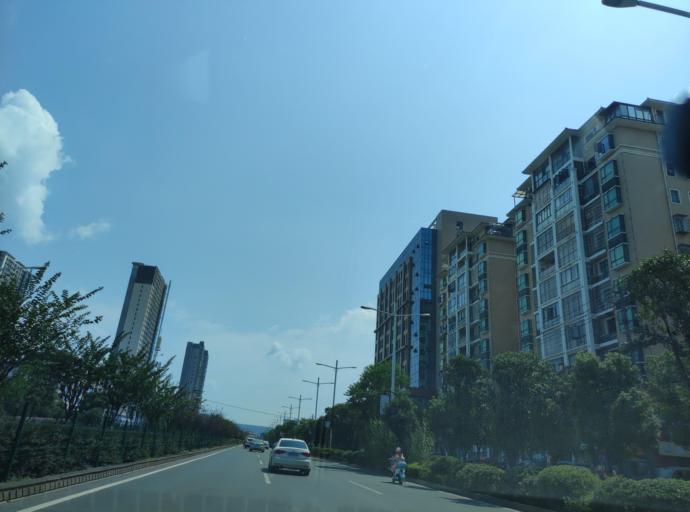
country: CN
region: Jiangxi Sheng
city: Pingxiang
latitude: 27.6536
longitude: 113.8855
